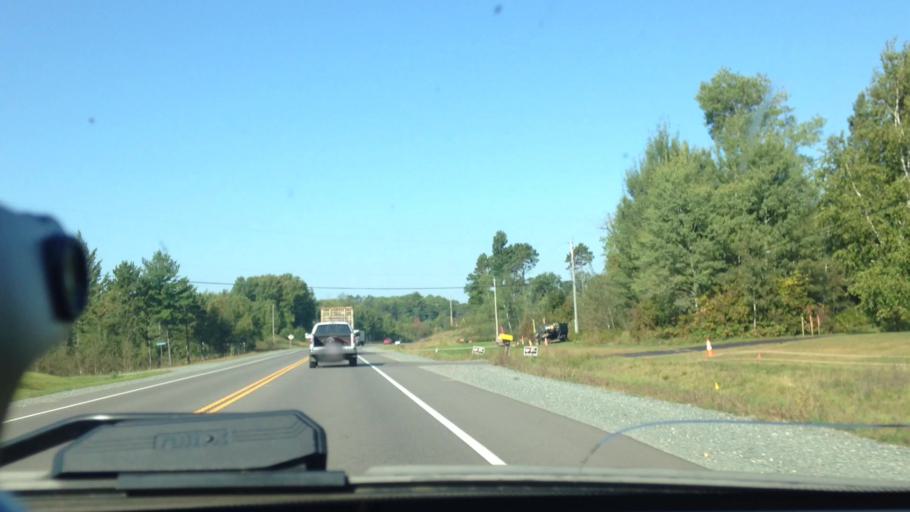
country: US
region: Michigan
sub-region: Dickinson County
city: Iron Mountain
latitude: 45.8760
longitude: -88.1104
